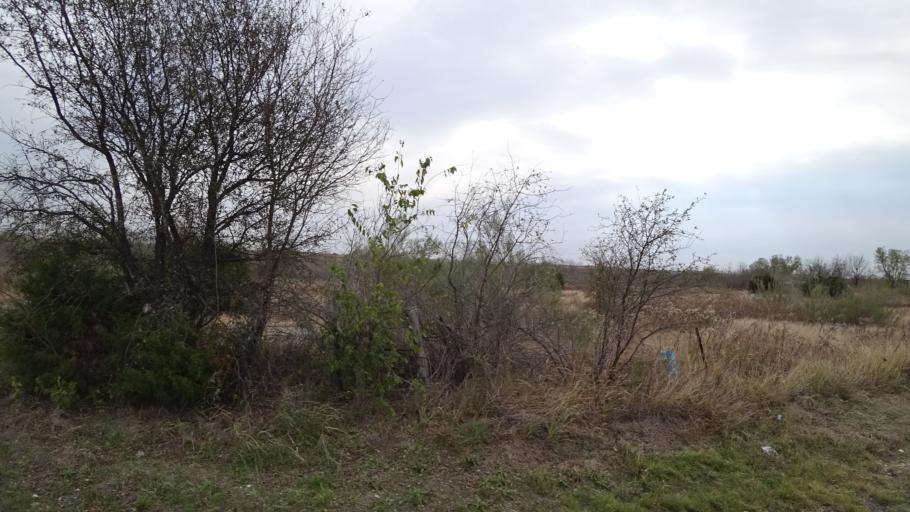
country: US
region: Texas
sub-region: Travis County
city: Garfield
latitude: 30.1524
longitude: -97.6627
